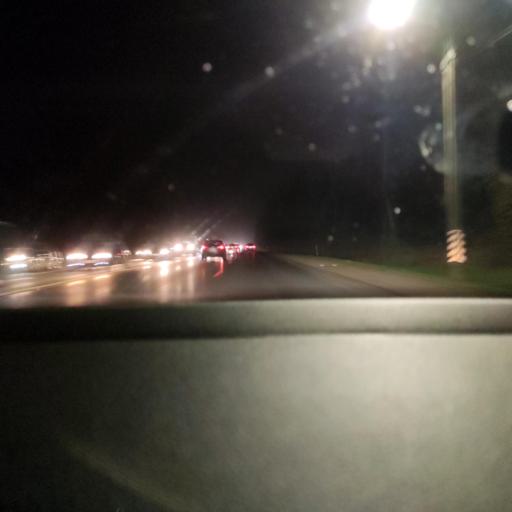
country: RU
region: Moskovskaya
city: Kievskij
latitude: 55.3974
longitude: 36.8052
